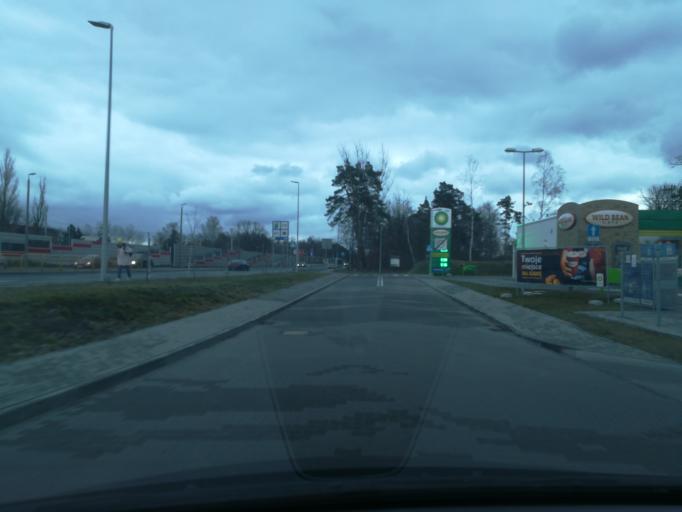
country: PL
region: Kujawsko-Pomorskie
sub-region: Torun
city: Torun
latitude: 52.9919
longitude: 18.6361
